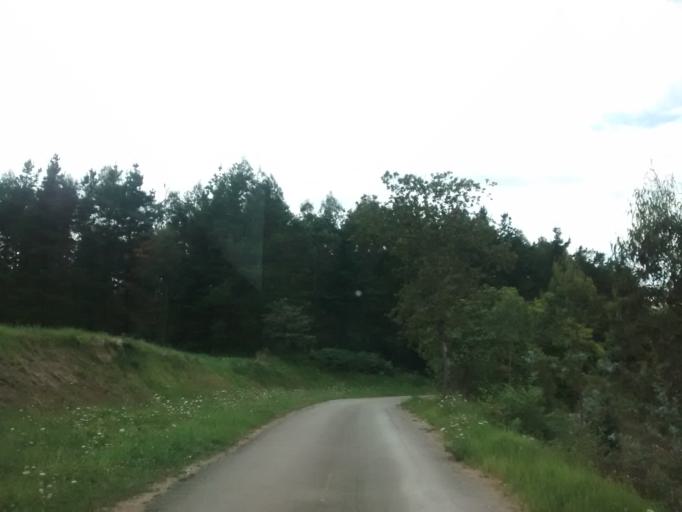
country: ES
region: Cantabria
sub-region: Provincia de Cantabria
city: Comillas
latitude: 43.3372
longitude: -4.3136
